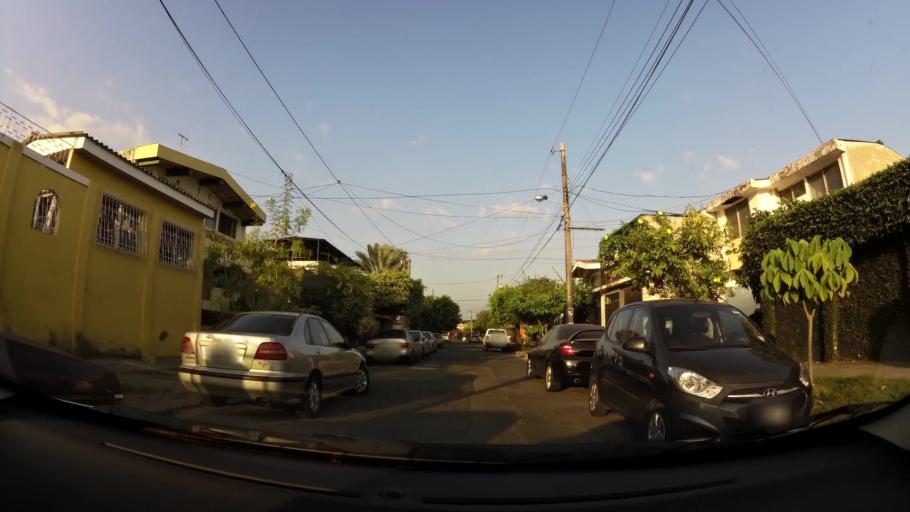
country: SV
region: San Salvador
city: Cuscatancingo
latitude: 13.7182
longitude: -89.1980
